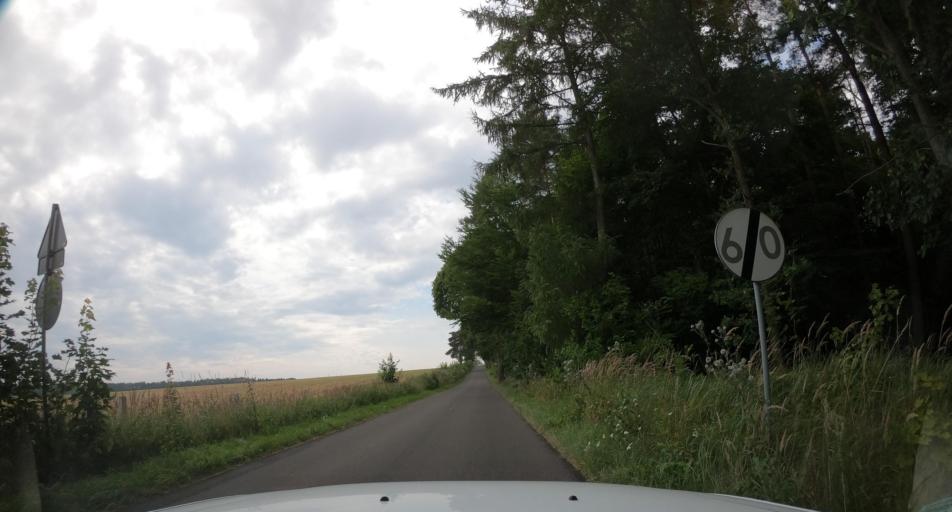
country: PL
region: West Pomeranian Voivodeship
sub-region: Powiat walecki
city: Walcz
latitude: 53.2352
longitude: 16.3308
